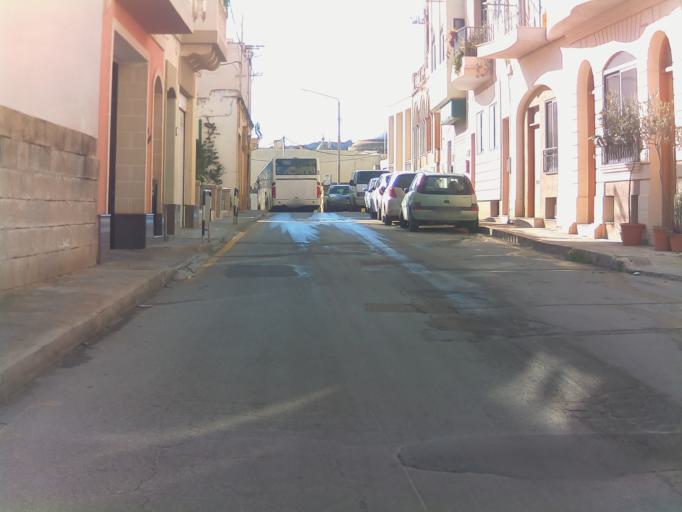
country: MT
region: L-Imgarr
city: Imgarr
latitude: 35.9225
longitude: 14.3670
